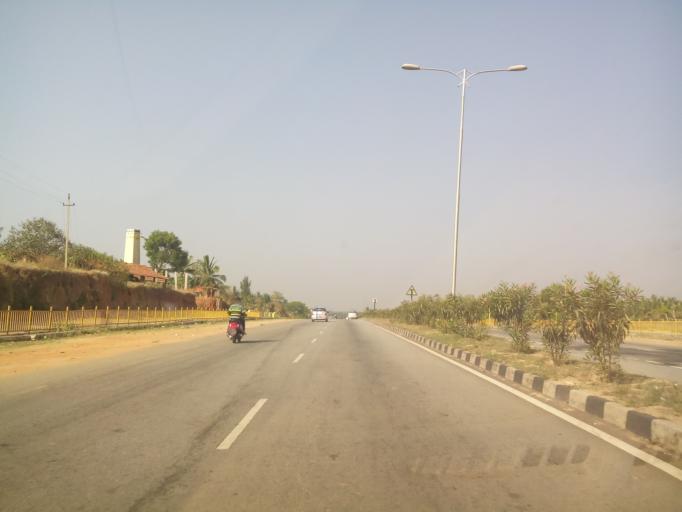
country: IN
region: Karnataka
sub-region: Ramanagara
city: Magadi
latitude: 13.0570
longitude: 77.1588
